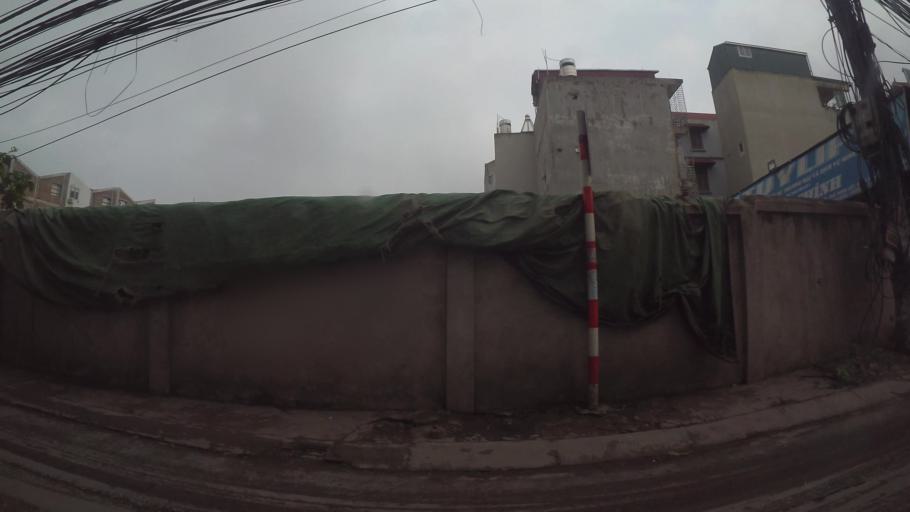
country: VN
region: Ha Noi
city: Van Dien
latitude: 20.9740
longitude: 105.8452
